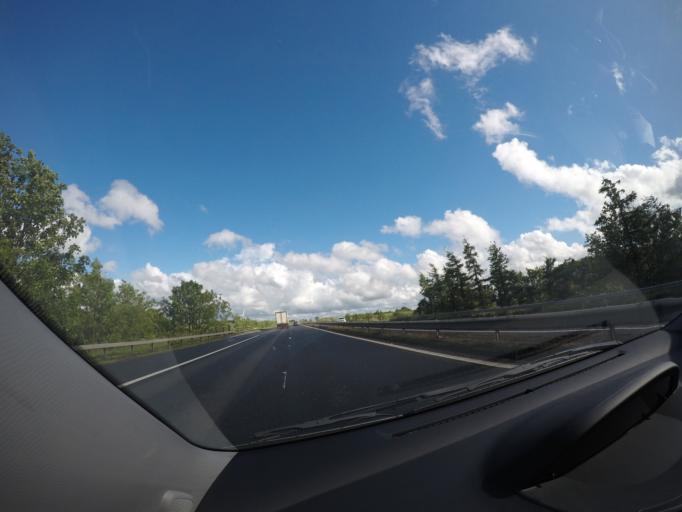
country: GB
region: Scotland
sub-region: South Lanarkshire
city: Lesmahagow
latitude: 55.6279
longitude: -3.8613
